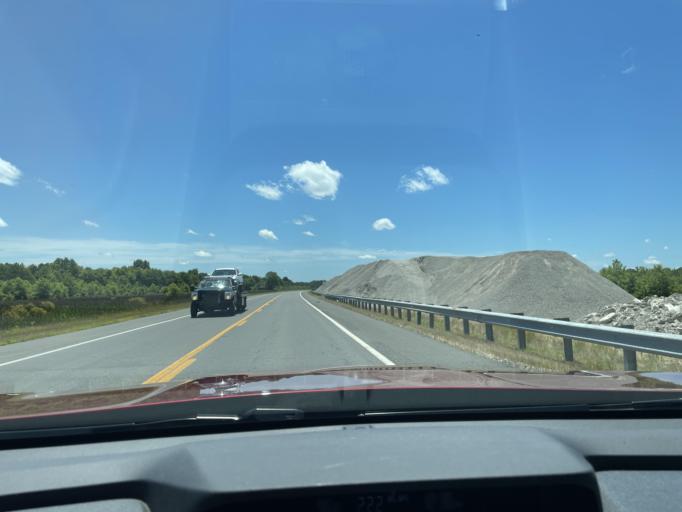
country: US
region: Arkansas
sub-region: Jefferson County
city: Pine Bluff
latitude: 34.1610
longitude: -91.9835
